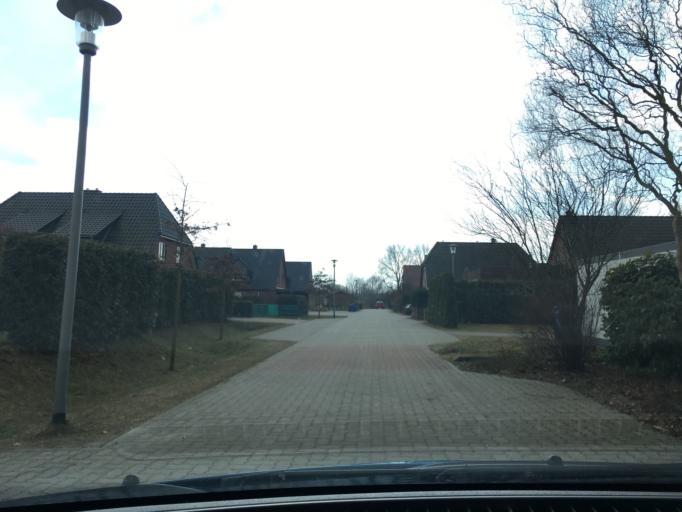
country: DE
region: Lower Saxony
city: Handorf
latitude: 53.3350
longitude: 10.3168
